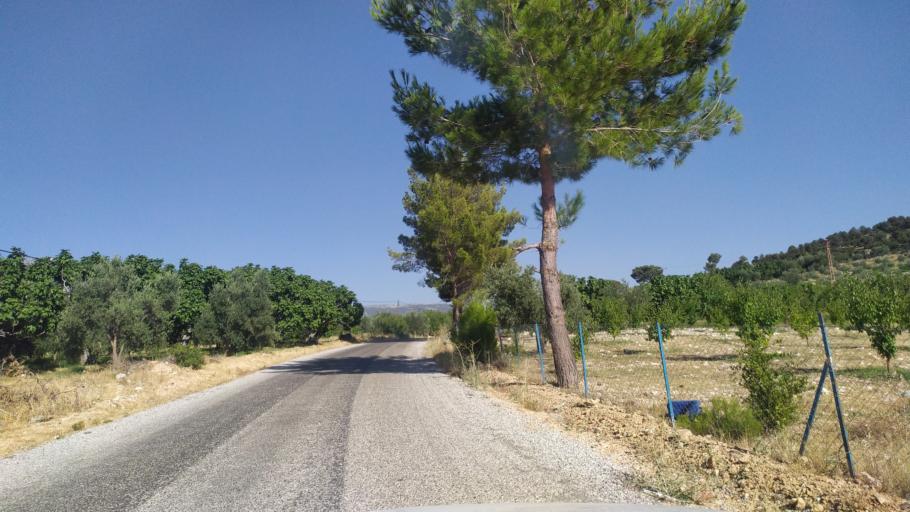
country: TR
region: Mersin
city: Mut
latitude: 36.7023
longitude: 33.4763
